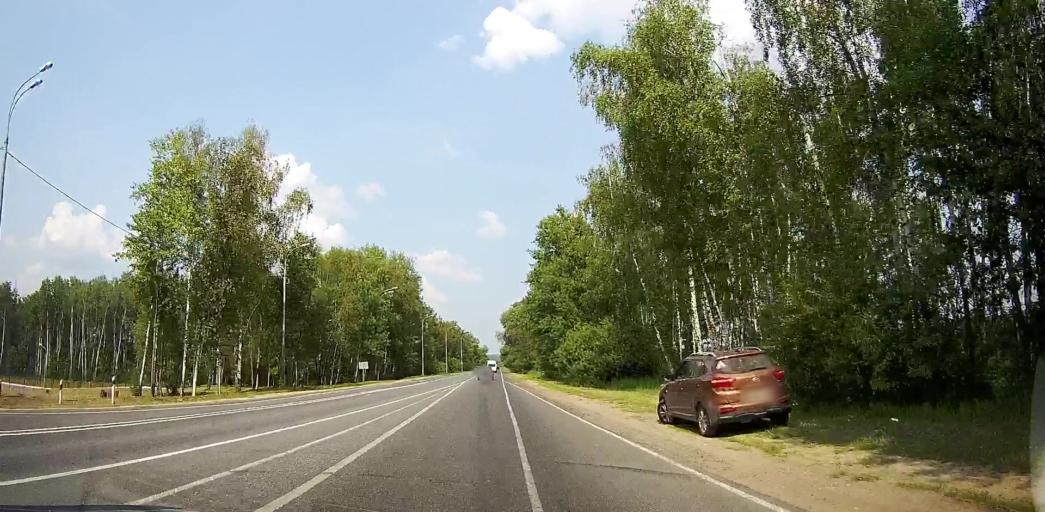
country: RU
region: Moskovskaya
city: Stupino
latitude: 54.9315
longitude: 38.1253
